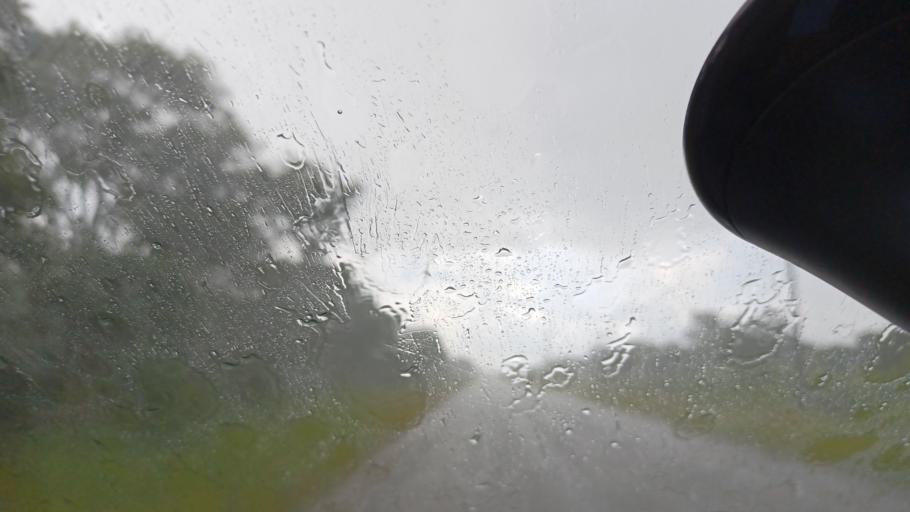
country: ZM
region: North-Western
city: Kasempa
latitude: -13.0944
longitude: 25.9169
